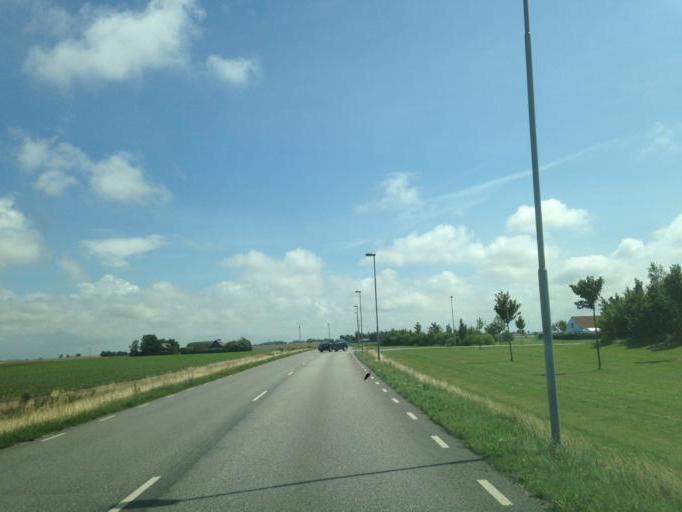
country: SE
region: Skane
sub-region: Trelleborgs Kommun
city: Skare
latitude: 55.4099
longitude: 13.0796
